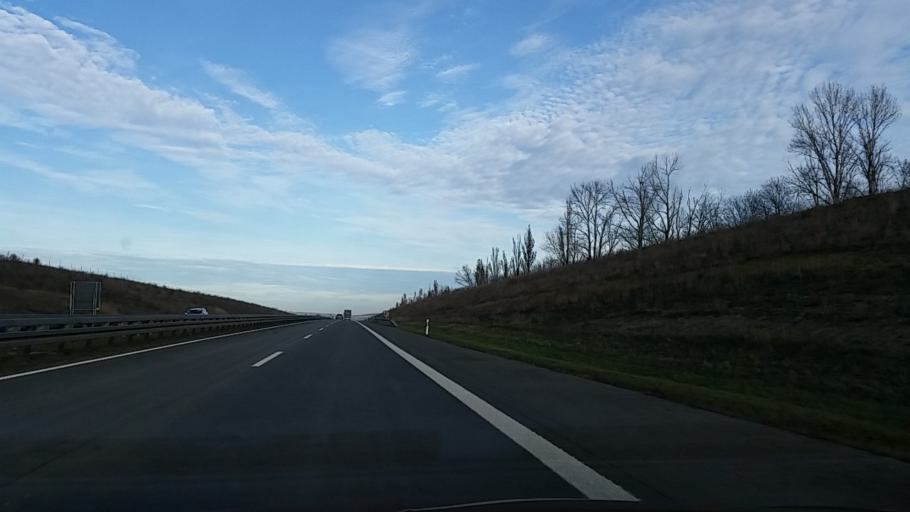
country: DE
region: Thuringia
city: Schillingstedt
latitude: 51.2145
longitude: 11.1853
